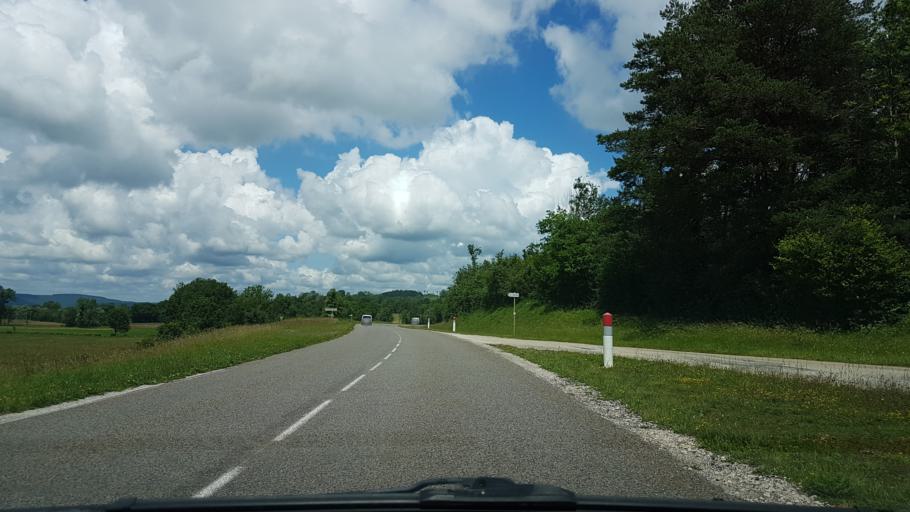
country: FR
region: Franche-Comte
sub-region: Departement du Jura
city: Clairvaux-les-Lacs
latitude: 46.5543
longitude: 5.7454
